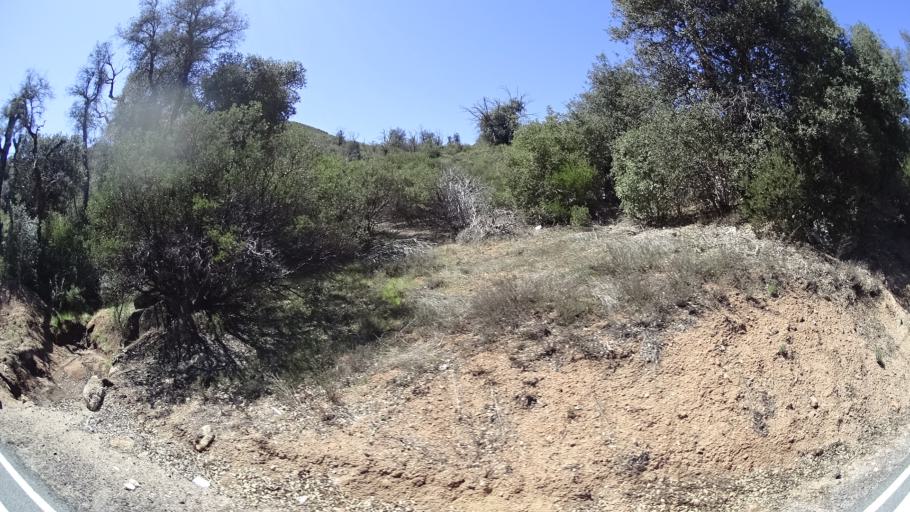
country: US
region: California
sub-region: San Diego County
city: Descanso
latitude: 32.8983
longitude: -116.5805
